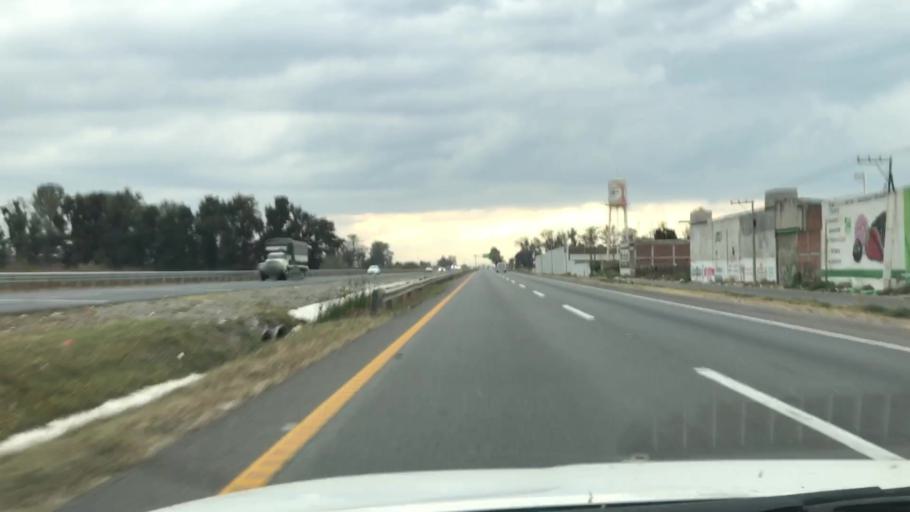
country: MX
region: Guanajuato
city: Irapuato
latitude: 20.6493
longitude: -101.3524
